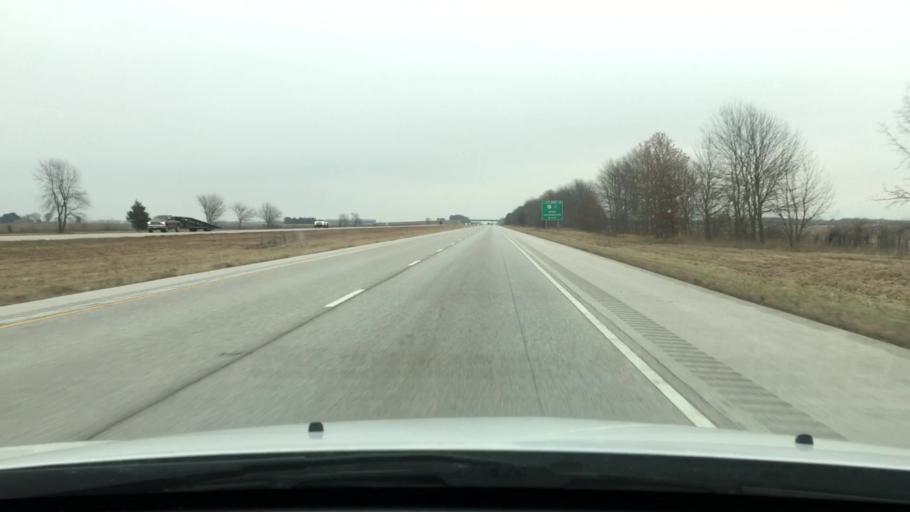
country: US
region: Illinois
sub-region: Morgan County
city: South Jacksonville
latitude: 39.6802
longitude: -90.3432
